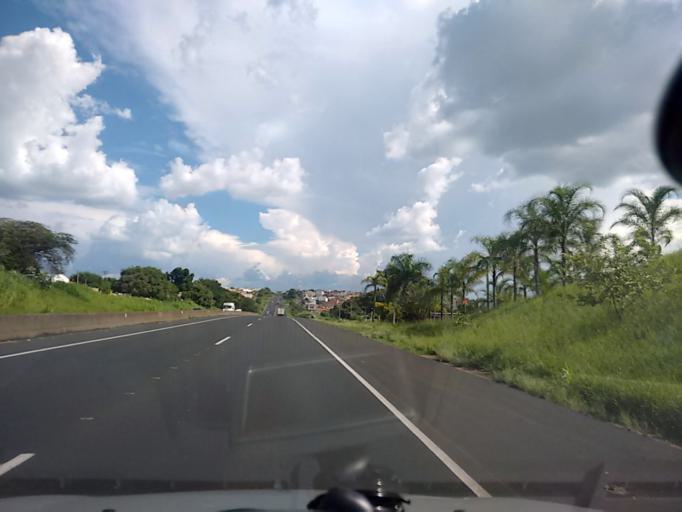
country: BR
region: Sao Paulo
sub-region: Marilia
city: Marilia
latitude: -22.1950
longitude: -49.9659
